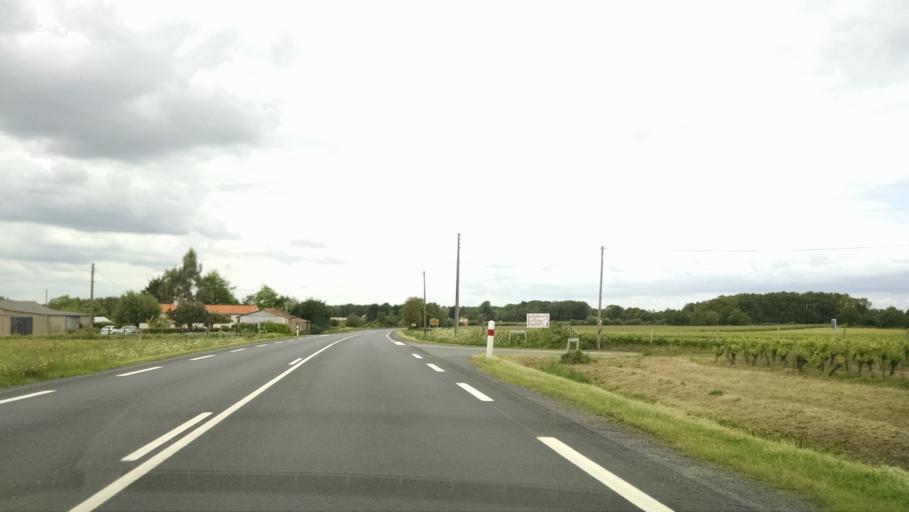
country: FR
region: Pays de la Loire
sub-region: Departement de la Loire-Atlantique
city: Le Bignon
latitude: 47.1051
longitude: -1.4667
